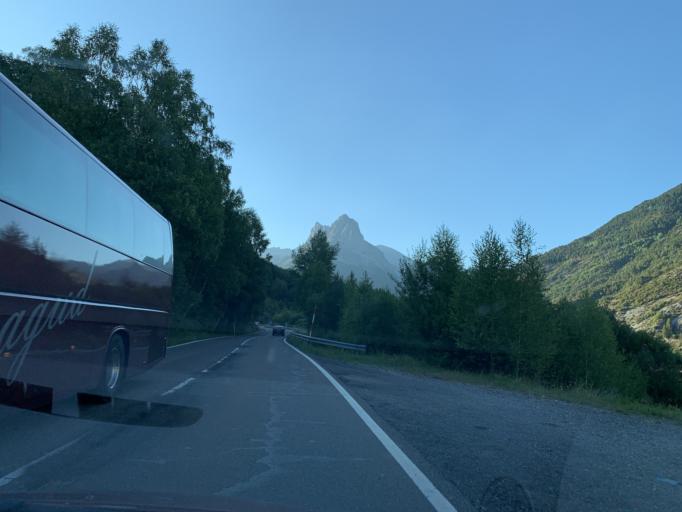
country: ES
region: Aragon
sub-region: Provincia de Huesca
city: Sallent de Gallego
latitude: 42.7526
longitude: -0.3178
